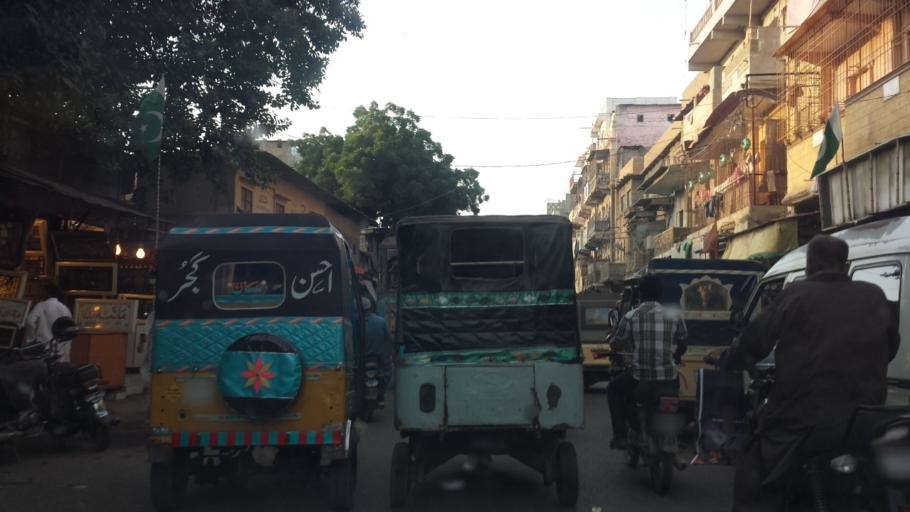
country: PK
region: Sindh
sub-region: Karachi District
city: Karachi
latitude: 24.8568
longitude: 67.0151
